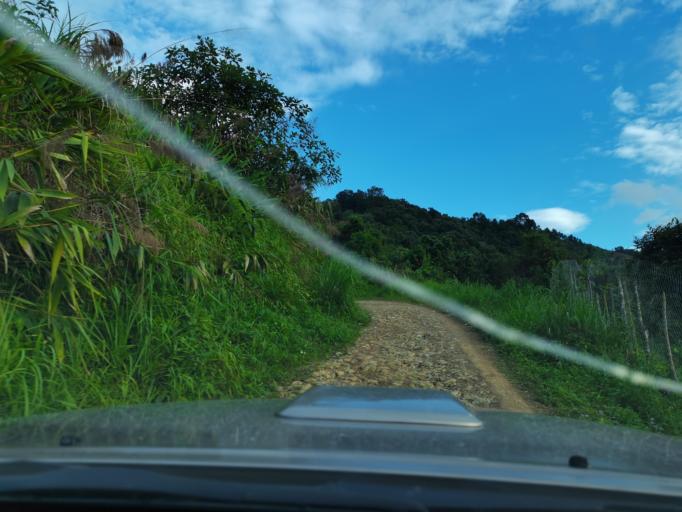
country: LA
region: Phongsali
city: Phongsali
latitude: 21.6757
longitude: 102.1886
